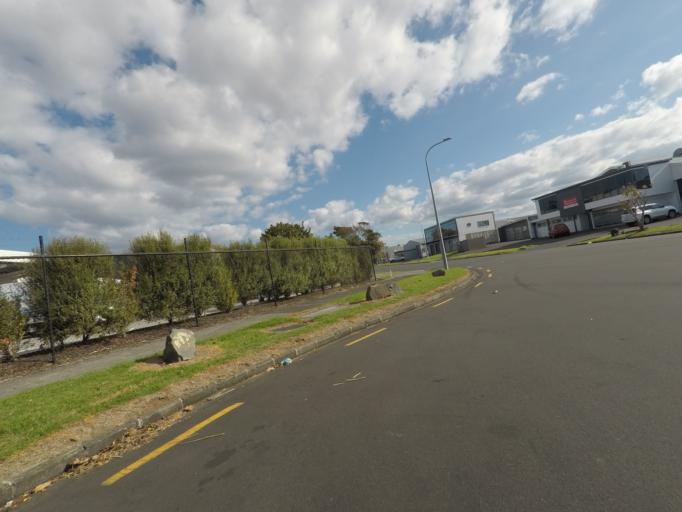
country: NZ
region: Auckland
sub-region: Auckland
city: Rosebank
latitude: -36.8817
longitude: 174.6823
